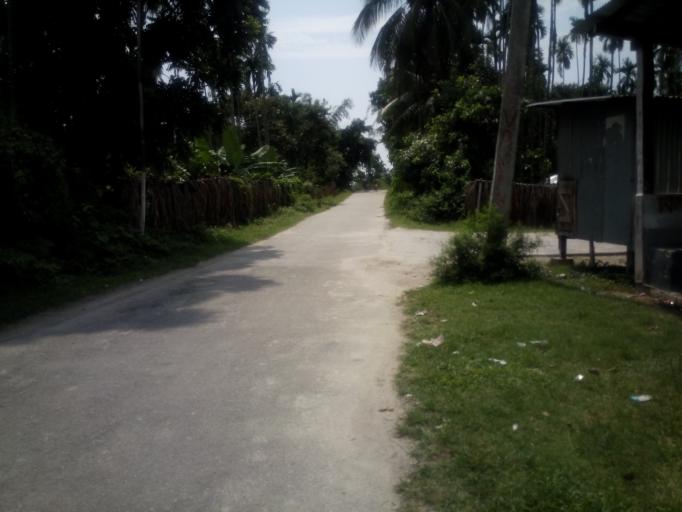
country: IN
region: Assam
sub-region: Udalguri
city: Udalguri
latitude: 26.7372
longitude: 92.1418
